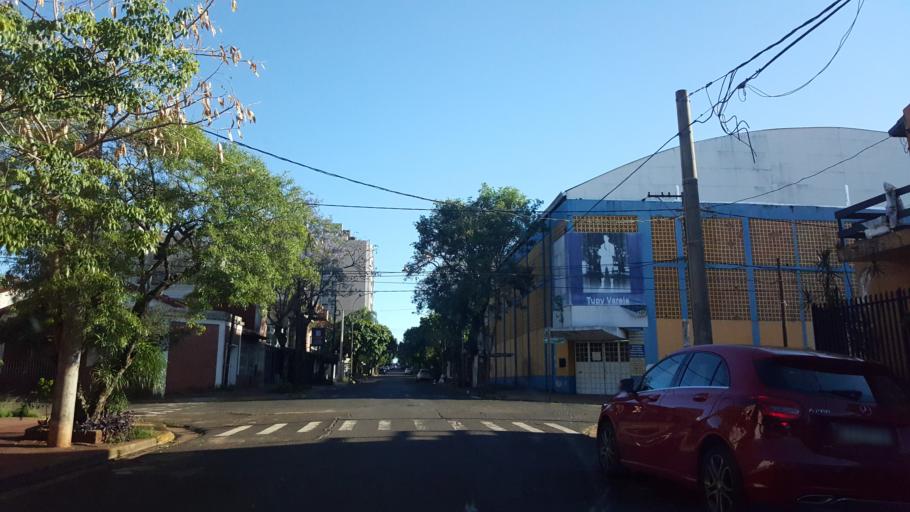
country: AR
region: Misiones
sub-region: Departamento de Capital
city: Posadas
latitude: -27.3679
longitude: -55.9001
